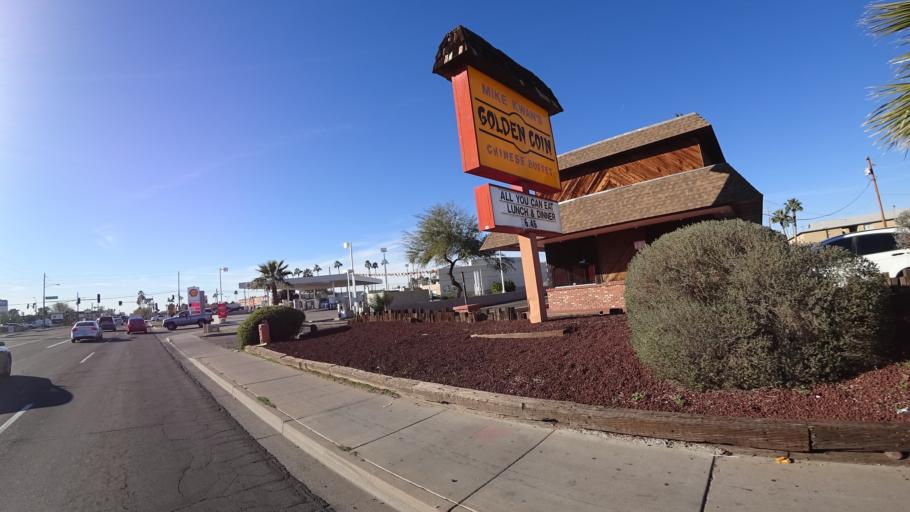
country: US
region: Arizona
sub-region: Maricopa County
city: Phoenix
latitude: 33.4806
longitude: -112.0114
